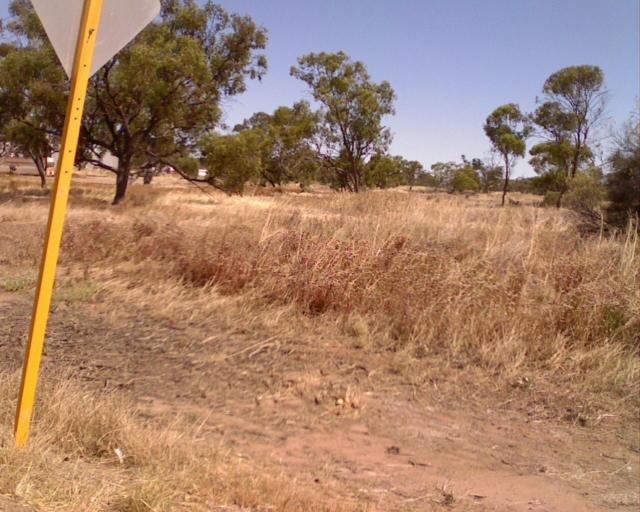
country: AU
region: Western Australia
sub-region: Moora
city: Moora
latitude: -30.3002
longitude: 116.0566
